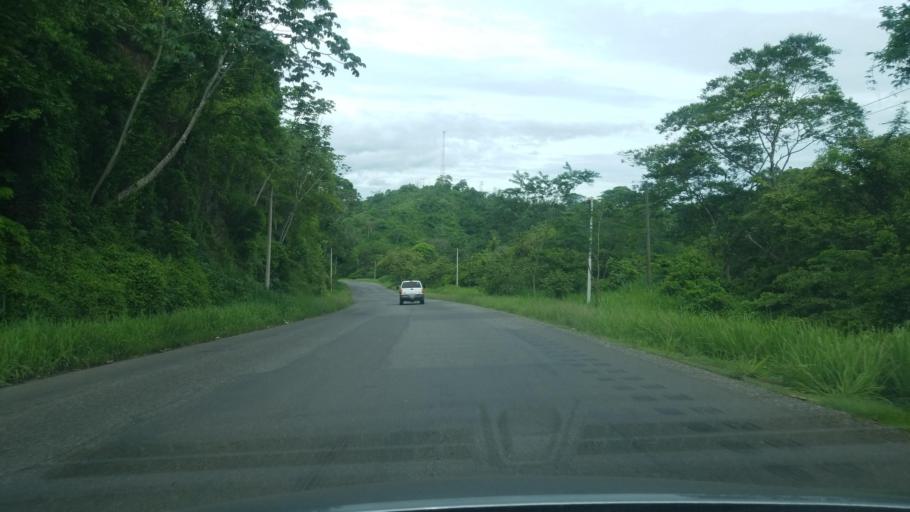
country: HN
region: Santa Barbara
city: Camalote
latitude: 15.3308
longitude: -88.3007
